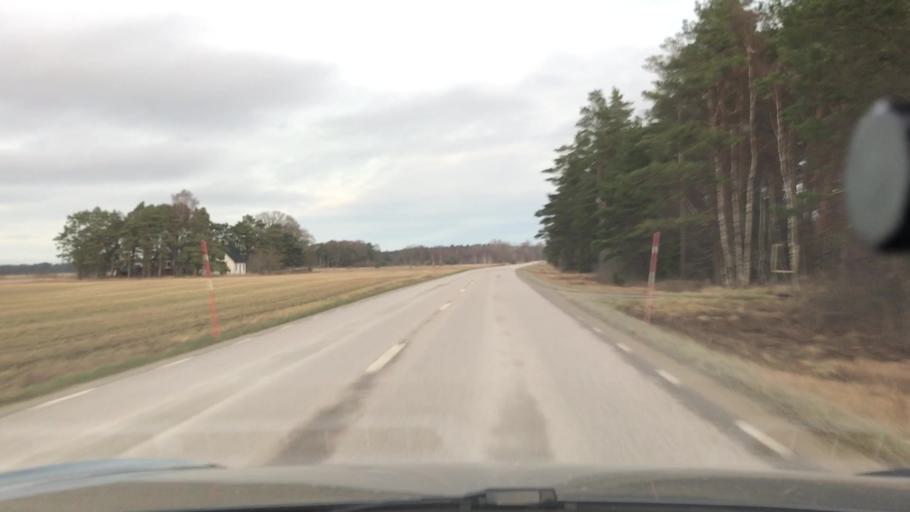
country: SE
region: Gotland
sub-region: Gotland
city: Slite
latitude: 57.7171
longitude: 18.5530
